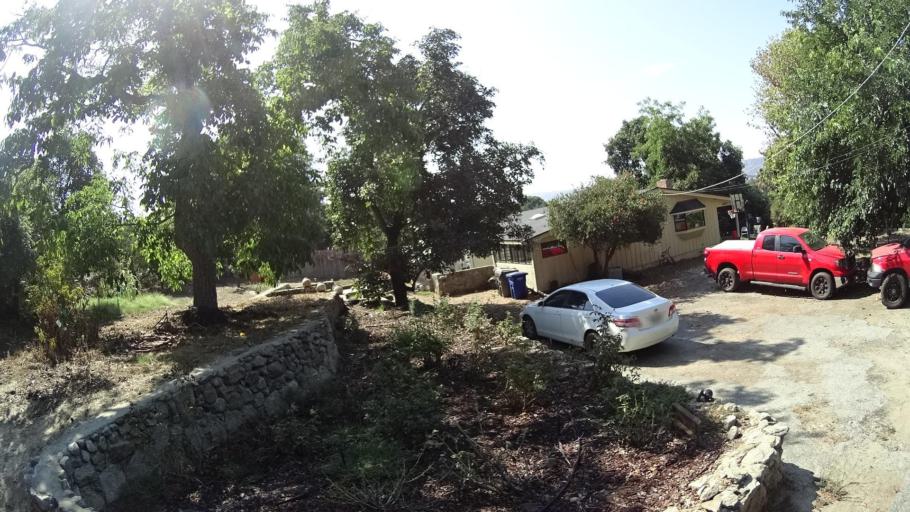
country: US
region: California
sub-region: San Diego County
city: Valley Center
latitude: 33.3375
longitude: -117.0014
